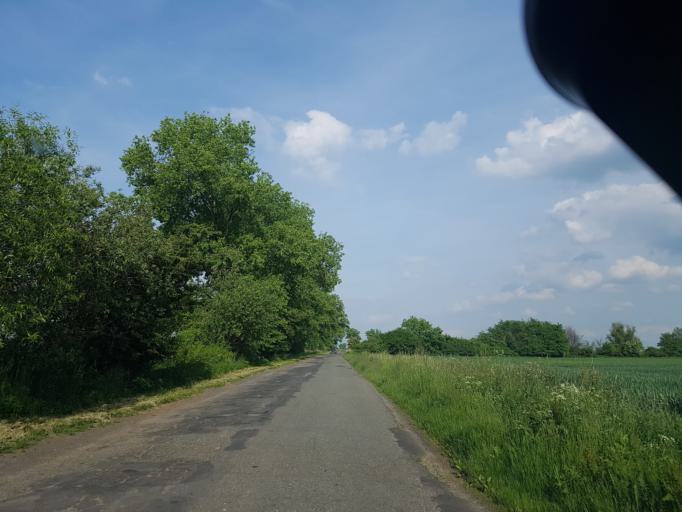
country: PL
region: Lower Silesian Voivodeship
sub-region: Powiat strzelinski
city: Wiazow
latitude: 50.8650
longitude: 17.1676
